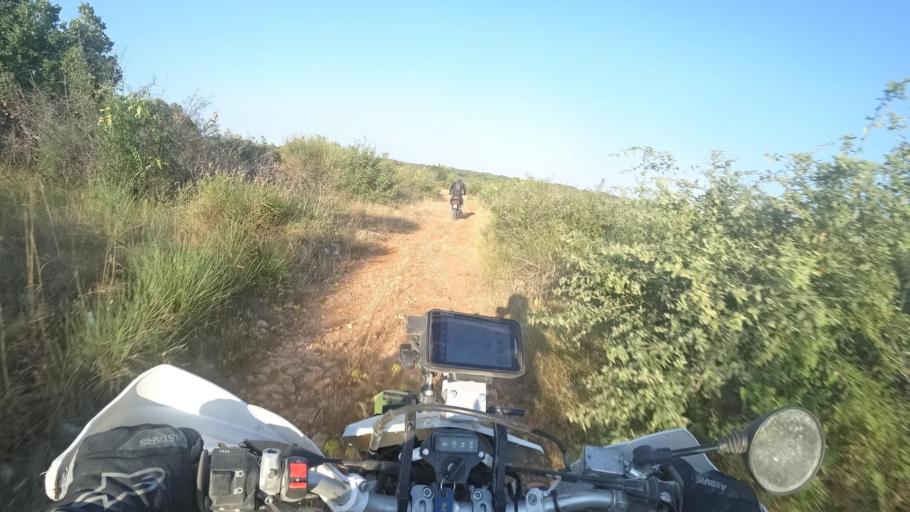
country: HR
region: Istarska
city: Galizana
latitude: 44.9489
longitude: 13.9013
